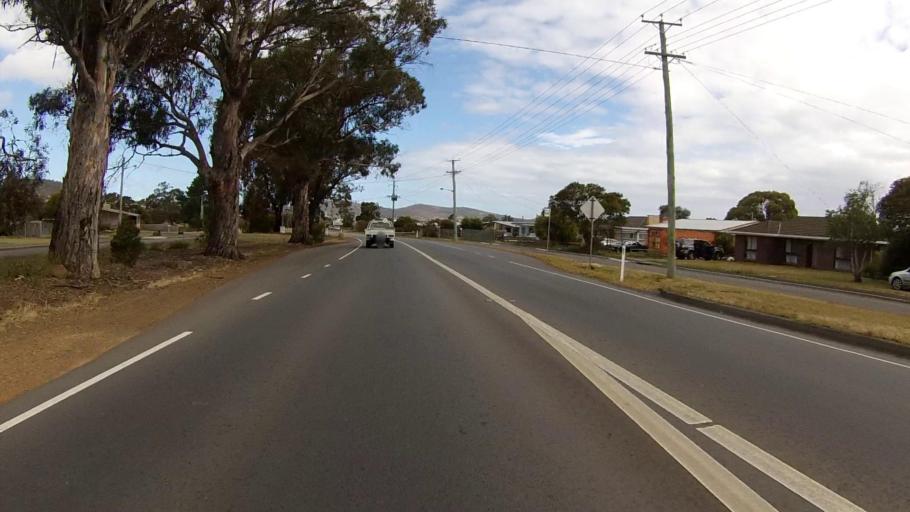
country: AU
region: Tasmania
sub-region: Clarence
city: Rokeby
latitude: -42.8953
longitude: 147.4382
